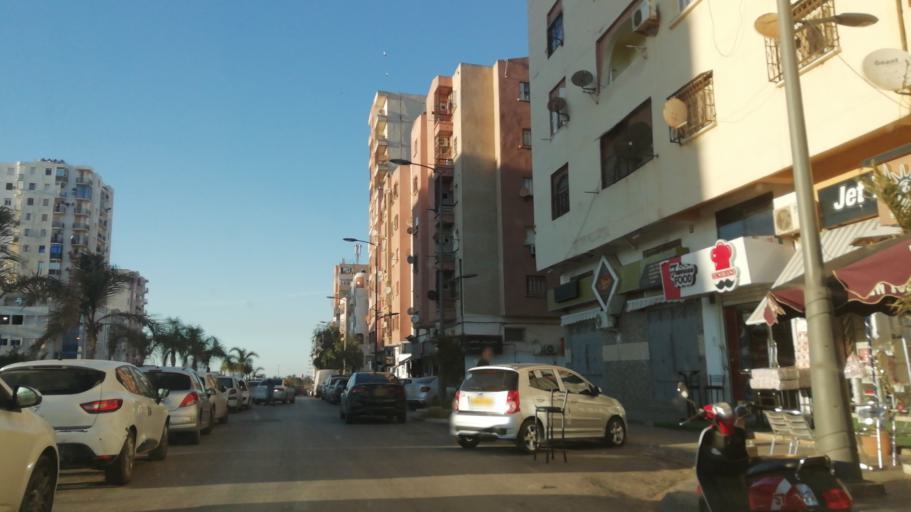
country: DZ
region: Oran
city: Bir el Djir
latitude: 35.7212
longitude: -0.5914
